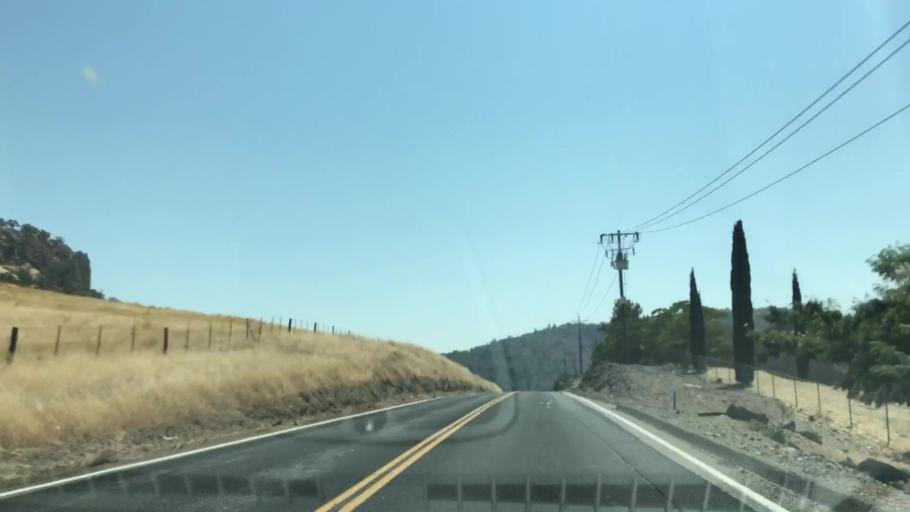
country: US
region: California
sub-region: Calaveras County
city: Copperopolis
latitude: 37.9025
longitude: -120.5810
